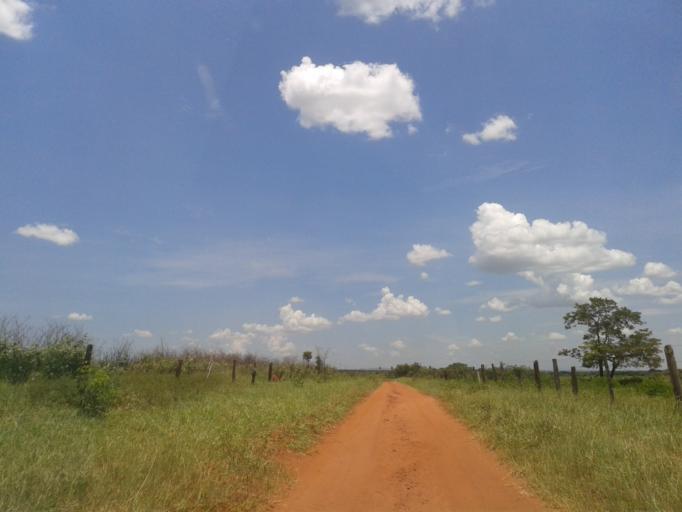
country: BR
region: Minas Gerais
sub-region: Santa Vitoria
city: Santa Vitoria
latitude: -19.2249
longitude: -50.4454
